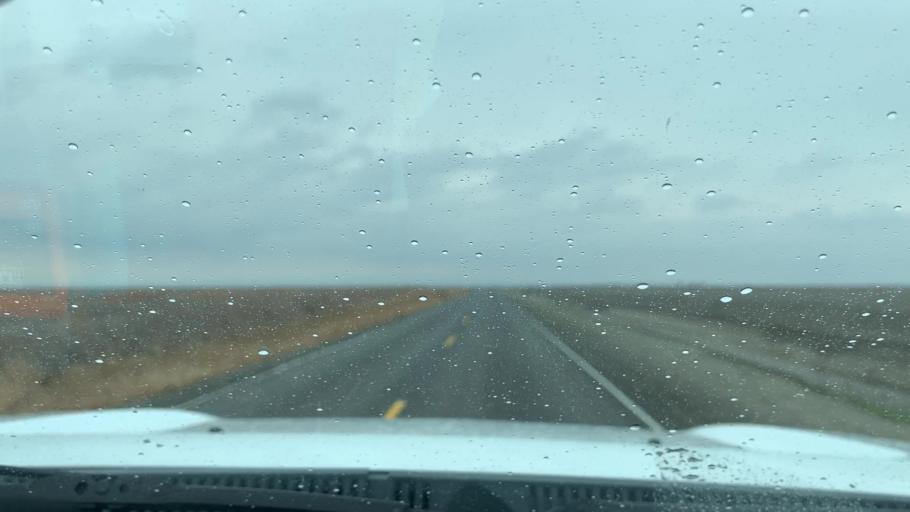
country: US
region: California
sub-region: Kings County
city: Kettleman City
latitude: 35.9340
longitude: -119.7483
